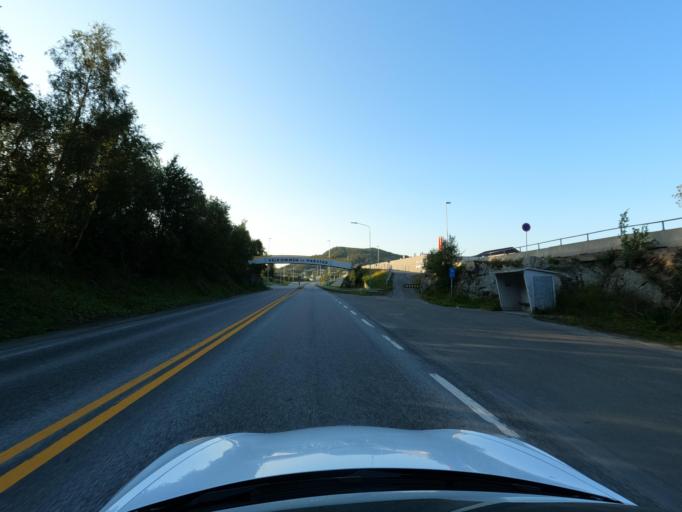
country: NO
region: Troms
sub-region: Harstad
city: Harstad
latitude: 68.7781
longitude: 16.5637
